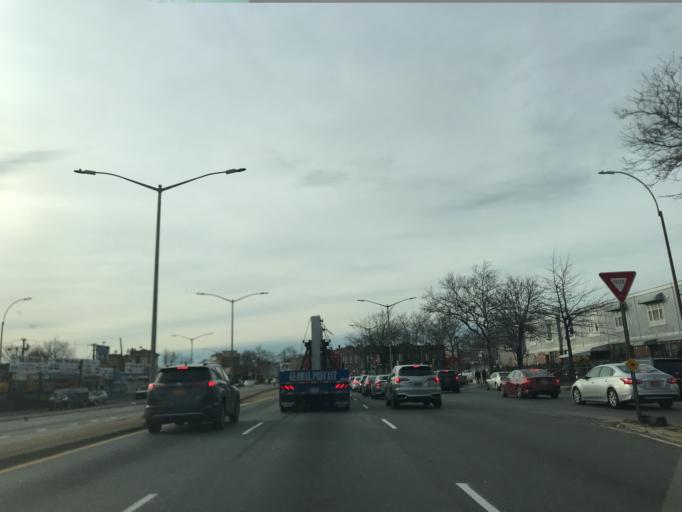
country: US
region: New York
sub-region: Kings County
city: East New York
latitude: 40.6577
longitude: -73.8946
